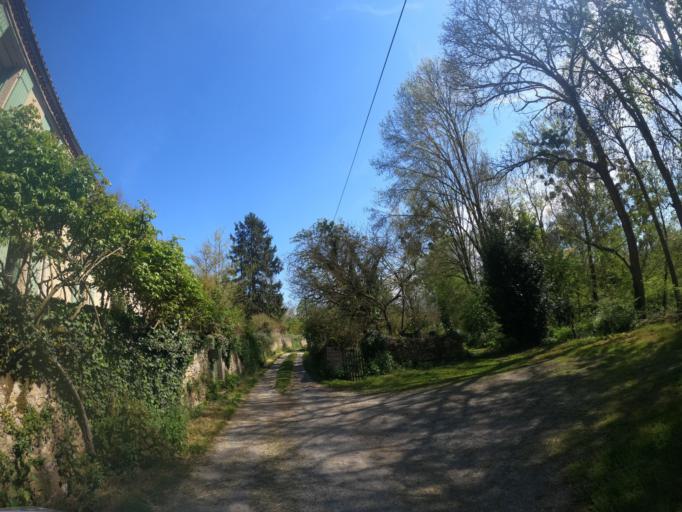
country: FR
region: Poitou-Charentes
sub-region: Departement des Deux-Sevres
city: Airvault
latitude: 46.8759
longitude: -0.1475
